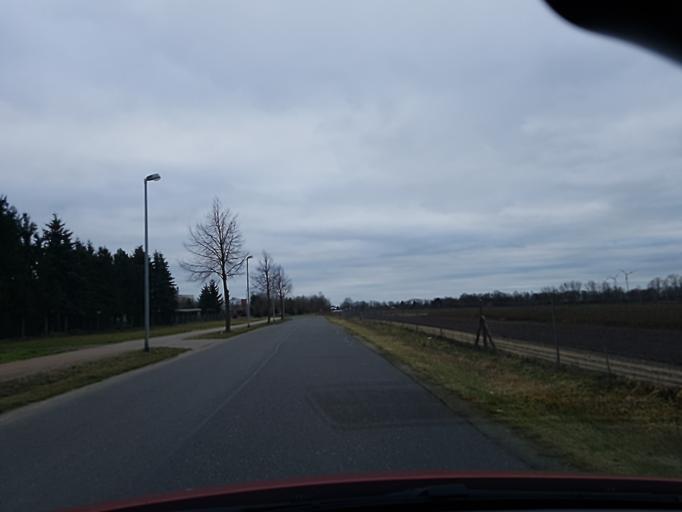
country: DE
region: Brandenburg
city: Elsterwerda
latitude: 51.4647
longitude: 13.4997
